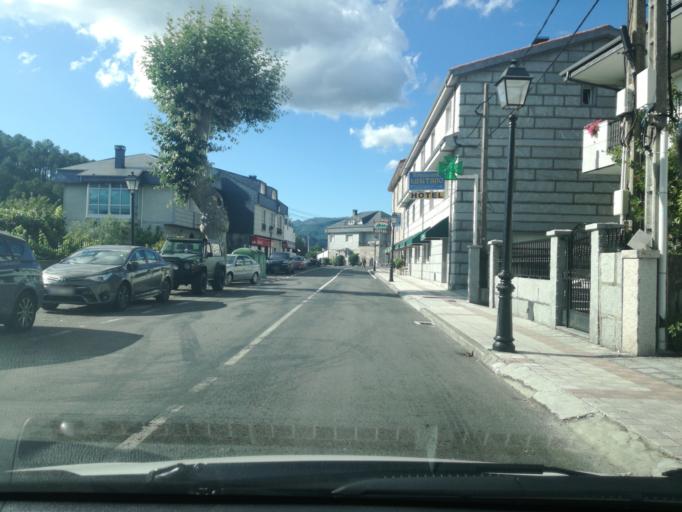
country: ES
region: Galicia
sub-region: Provincia de Ourense
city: Lobios
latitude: 41.9009
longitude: -8.0838
